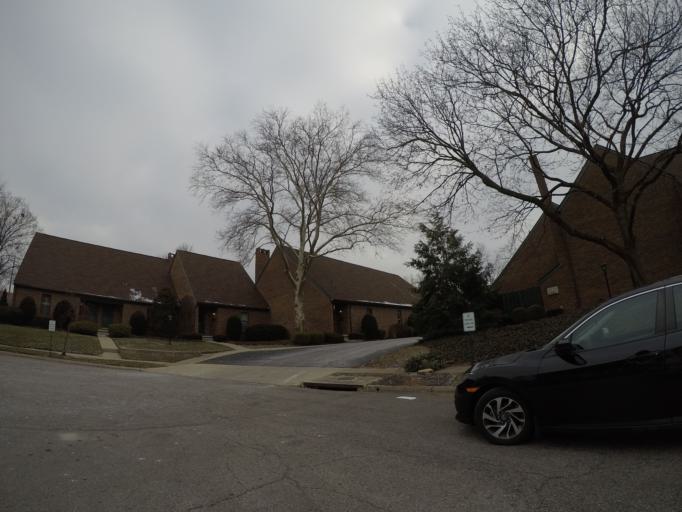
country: US
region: Ohio
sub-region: Franklin County
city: Upper Arlington
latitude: 40.0499
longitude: -83.0613
